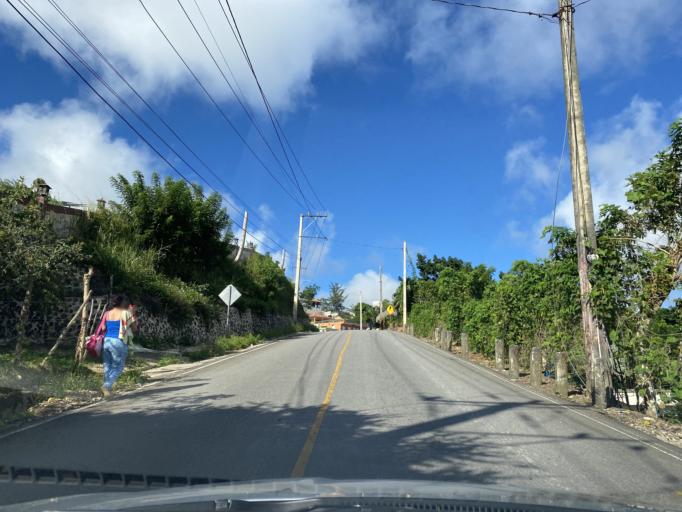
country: DO
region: Samana
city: Sanchez
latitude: 19.2564
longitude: -69.5711
